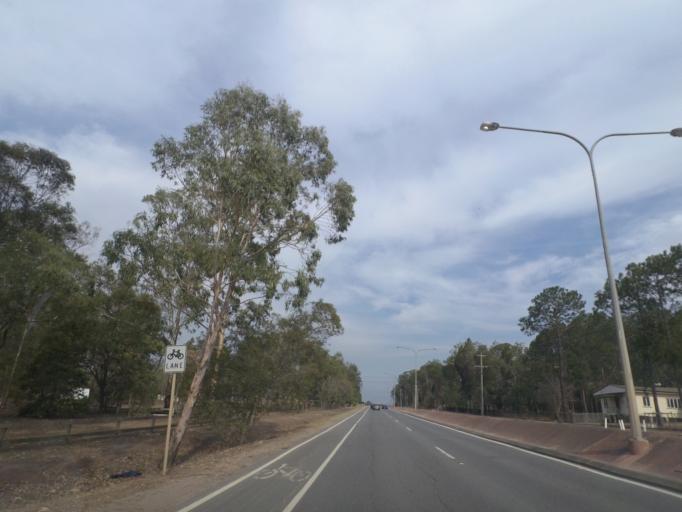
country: AU
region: Queensland
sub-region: Brisbane
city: Sunnybank
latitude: -27.5967
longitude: 153.0225
